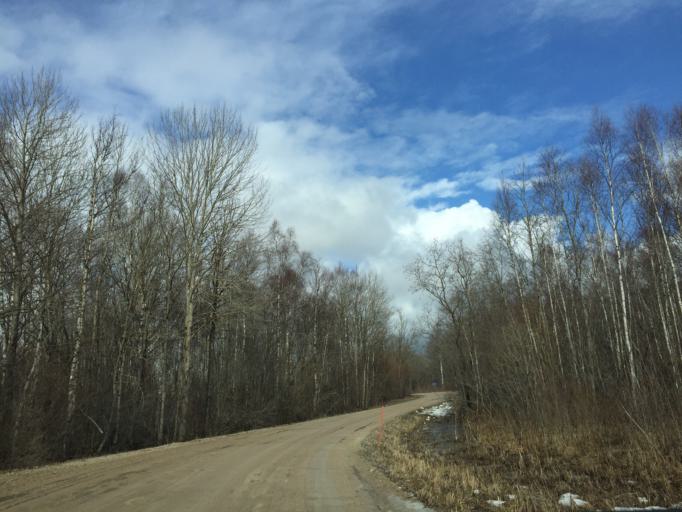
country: EE
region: Laeaene
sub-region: Lihula vald
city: Lihula
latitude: 58.7270
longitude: 23.8295
